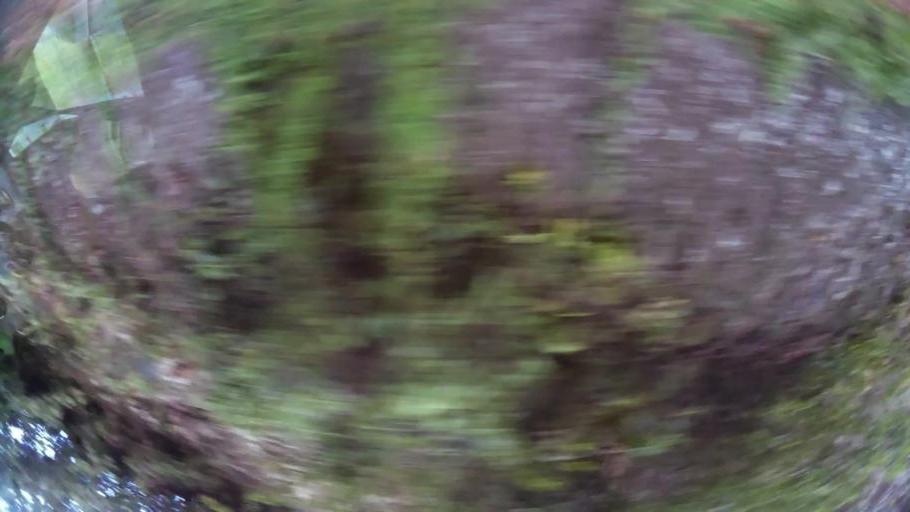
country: DM
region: Saint John
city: Portsmouth
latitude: 15.5842
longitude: -61.4102
